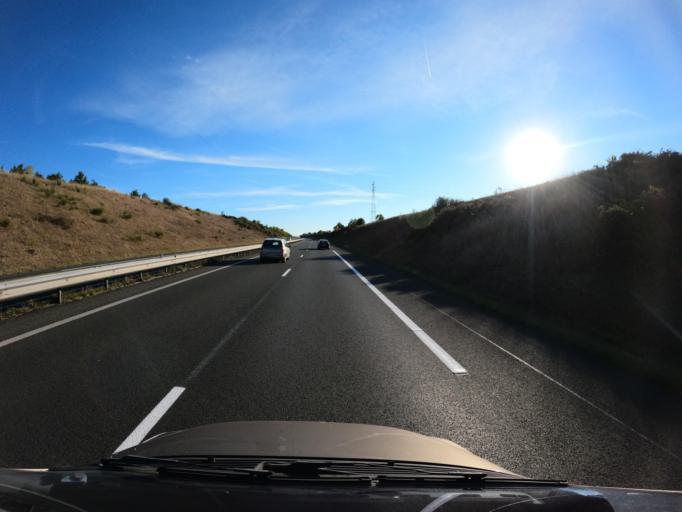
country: FR
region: Pays de la Loire
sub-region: Departement de Maine-et-Loire
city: Chemille-Melay
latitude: 47.2218
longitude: -0.7601
